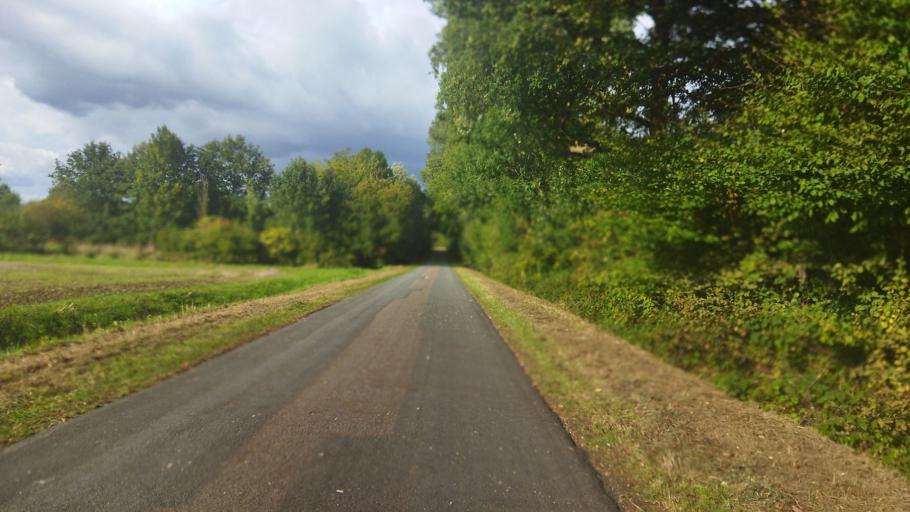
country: DE
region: North Rhine-Westphalia
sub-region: Regierungsbezirk Munster
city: Dulmen
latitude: 51.8744
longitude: 7.2629
